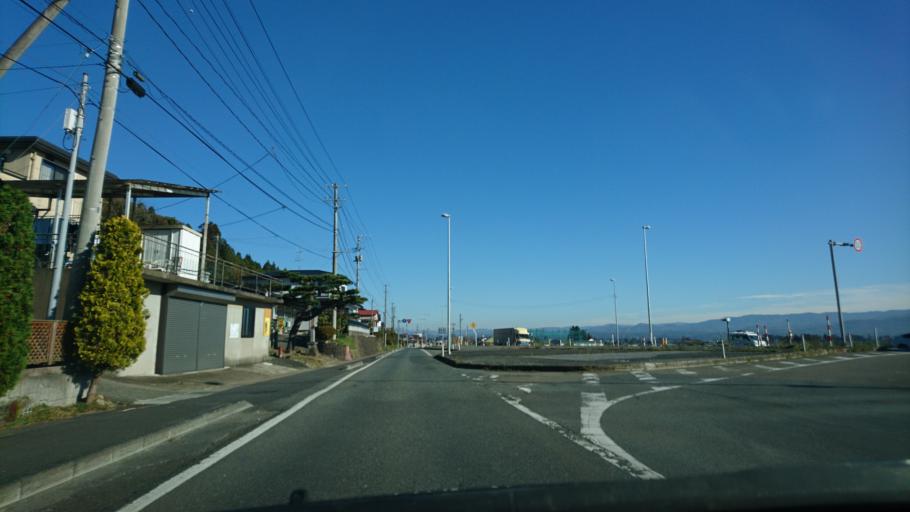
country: JP
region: Iwate
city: Mizusawa
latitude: 39.0731
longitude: 141.1308
